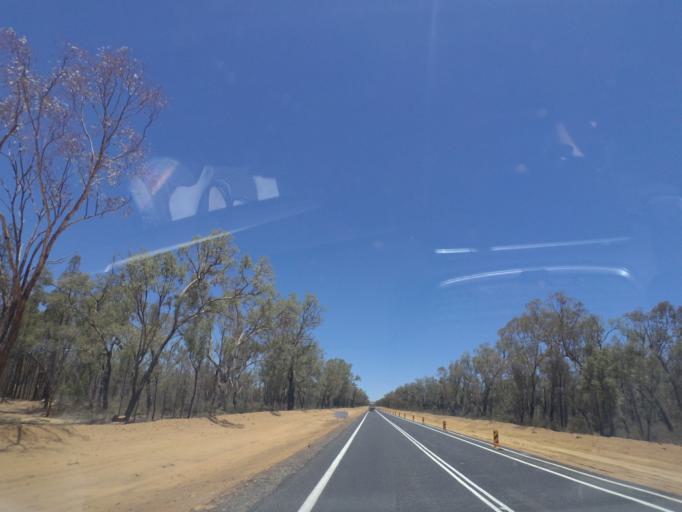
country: AU
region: New South Wales
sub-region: Warrumbungle Shire
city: Coonabarabran
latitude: -30.9313
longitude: 149.4285
